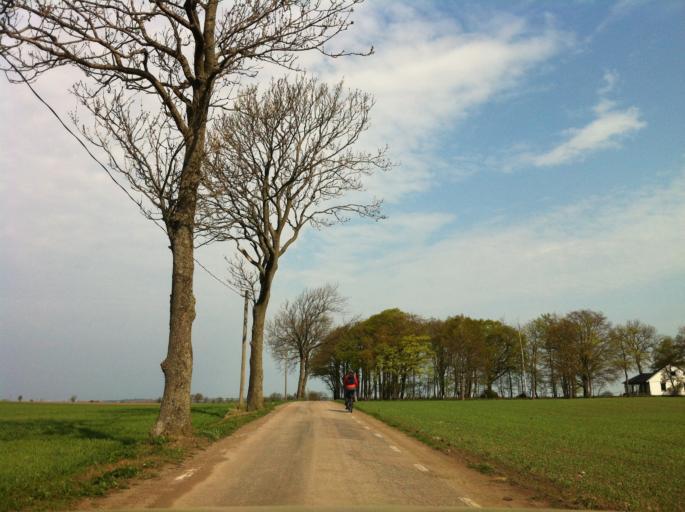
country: SE
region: Skane
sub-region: Helsingborg
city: Glumslov
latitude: 55.9444
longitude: 12.8394
